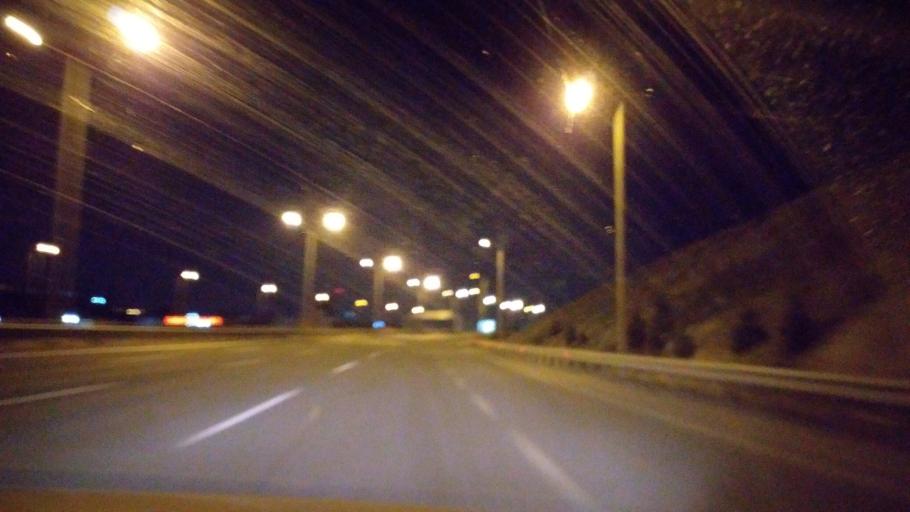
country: TR
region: Ankara
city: Ankara
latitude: 40.0206
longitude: 32.8236
